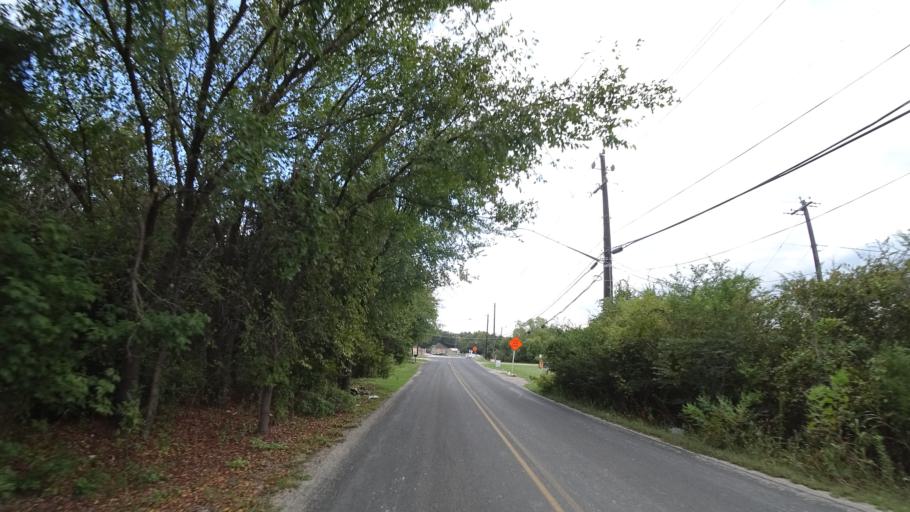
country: US
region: Texas
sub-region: Travis County
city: Onion Creek
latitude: 30.1868
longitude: -97.7941
